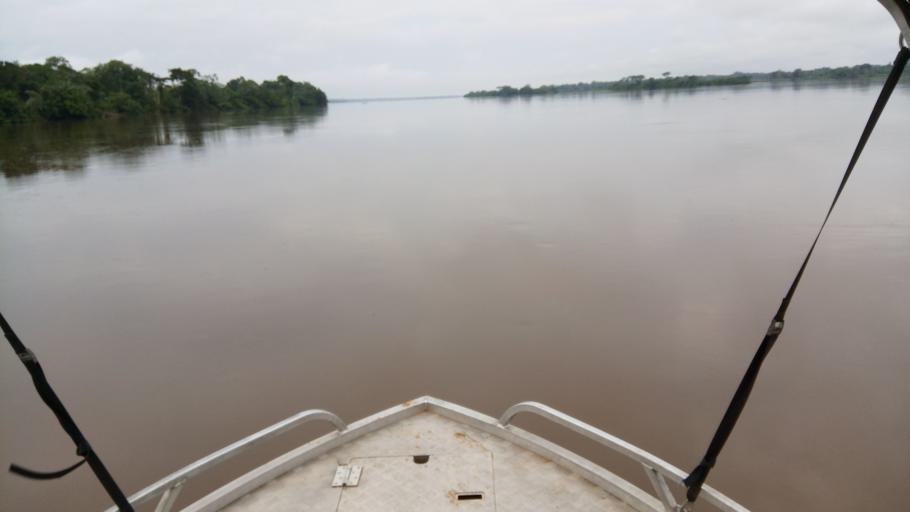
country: CD
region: Eastern Province
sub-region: Sous-Region de la Tshopo
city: Yangambi
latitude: 0.7560
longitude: 24.4387
